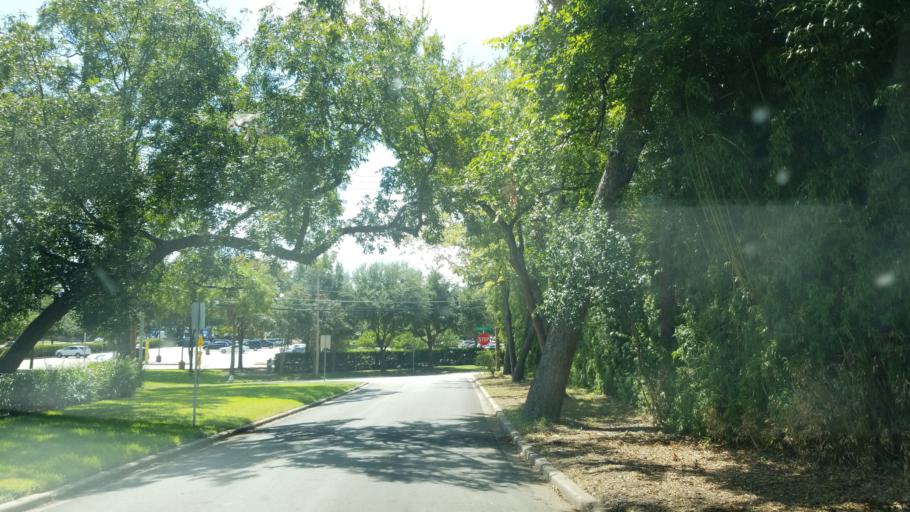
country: US
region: Texas
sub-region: Dallas County
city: Dallas
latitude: 32.7641
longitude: -96.8236
